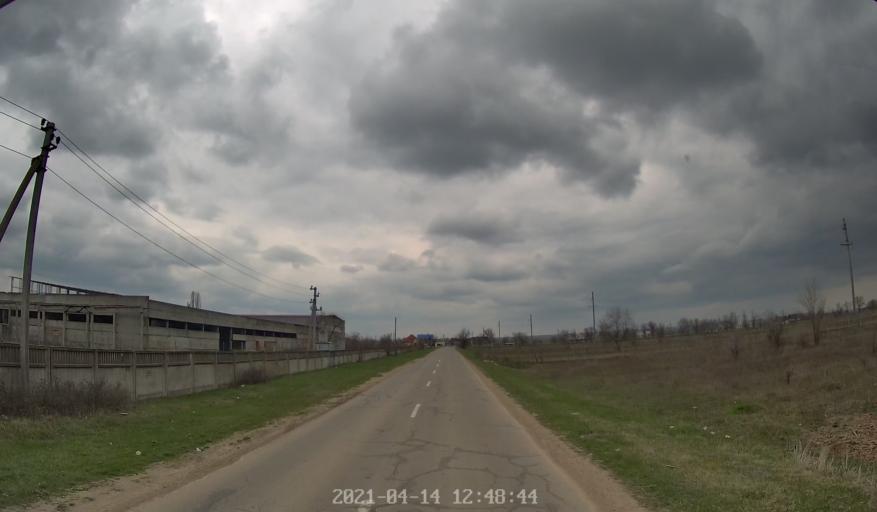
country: MD
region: Criuleni
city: Criuleni
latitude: 47.1536
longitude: 29.1529
